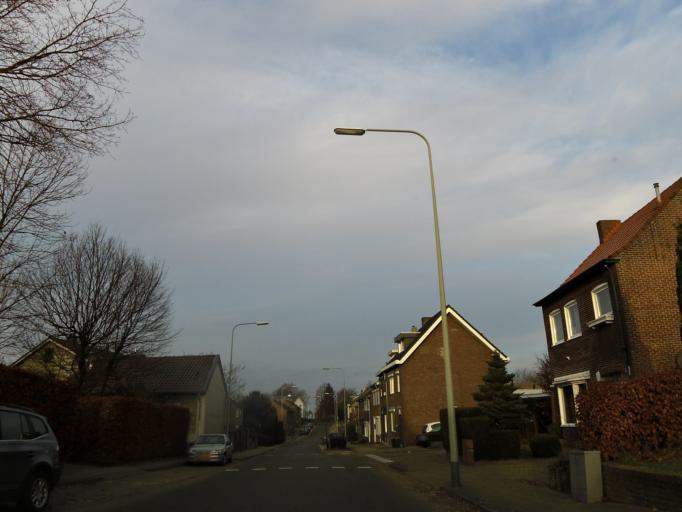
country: NL
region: Limburg
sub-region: Gemeente Simpelveld
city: Simpelveld
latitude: 50.8442
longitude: 5.9714
